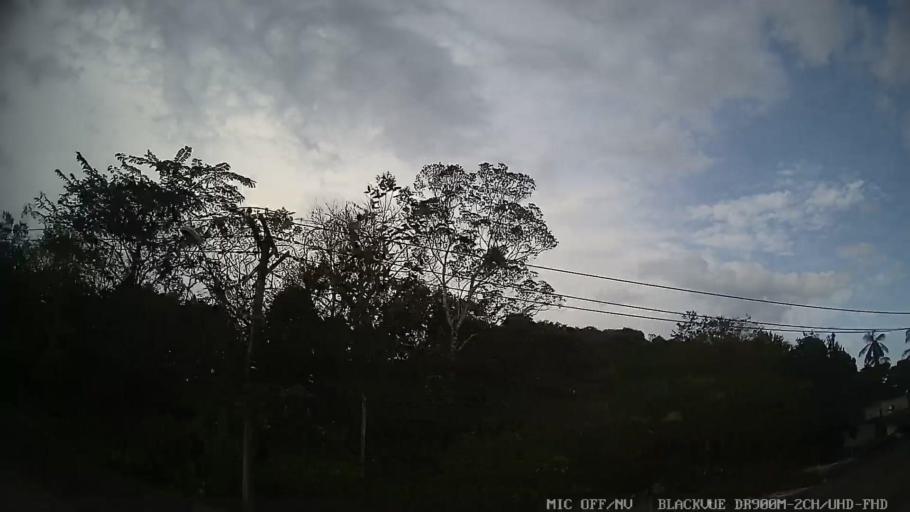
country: BR
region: Sao Paulo
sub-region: Santos
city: Santos
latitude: -23.9175
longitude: -46.2882
